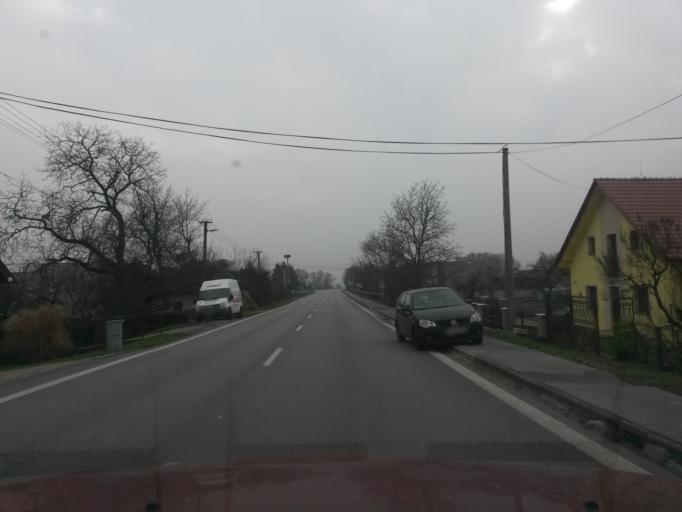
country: SK
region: Kosicky
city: Kosice
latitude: 48.8257
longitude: 21.2980
